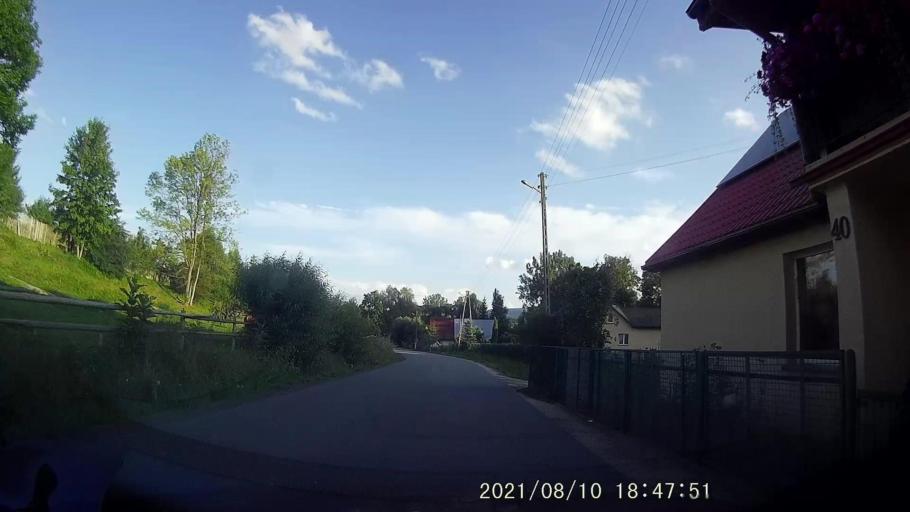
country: PL
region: Lower Silesian Voivodeship
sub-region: Powiat klodzki
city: Duszniki-Zdroj
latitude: 50.4312
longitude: 16.3589
